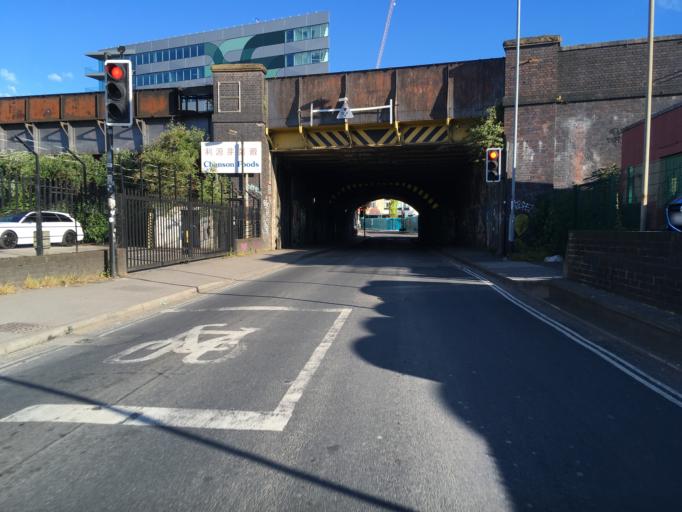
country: GB
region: England
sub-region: Bristol
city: Bristol
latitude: 51.4508
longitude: -2.5774
